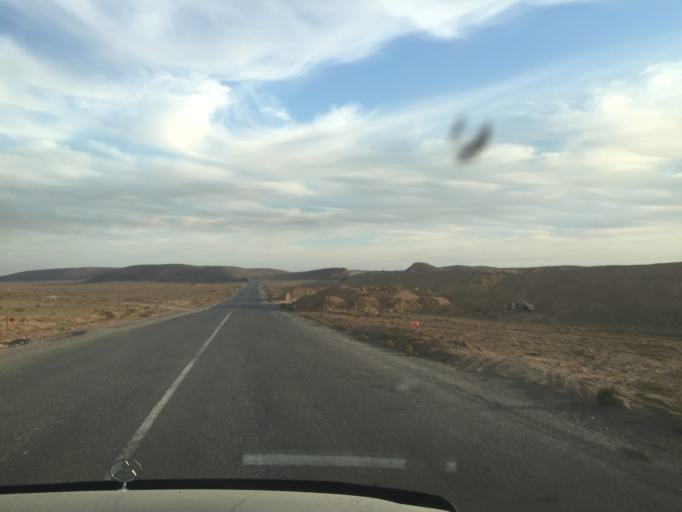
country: KZ
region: Almaty Oblysy
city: Ulken
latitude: 45.0672
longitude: 73.9972
